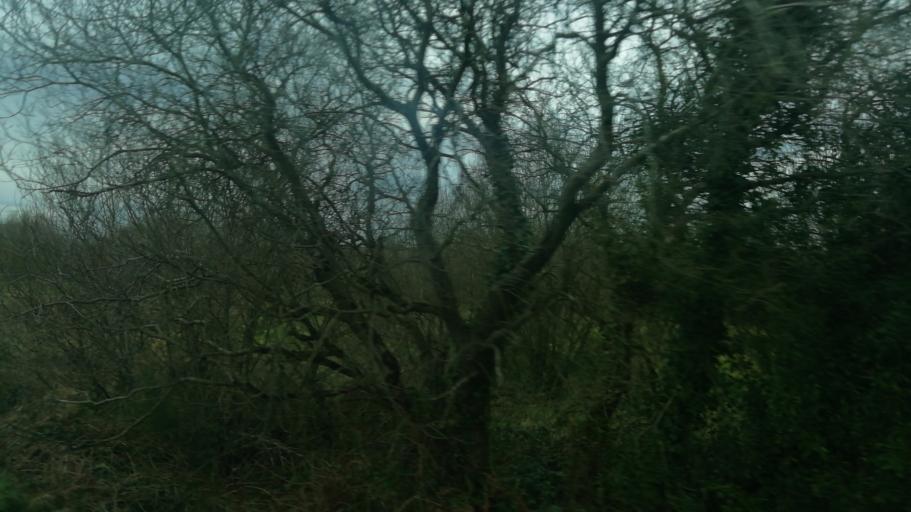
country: IE
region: Leinster
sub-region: Kildare
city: Derrinturn
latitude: 53.2822
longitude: -6.9063
